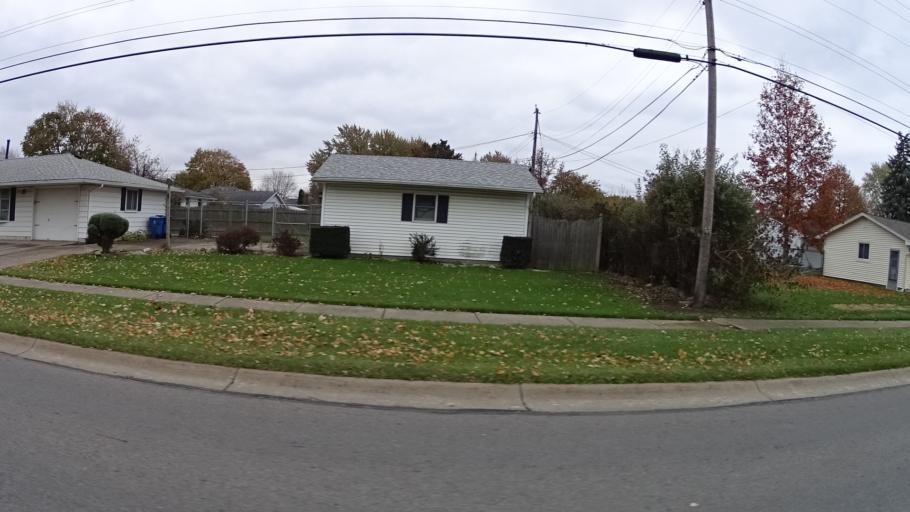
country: US
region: Ohio
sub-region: Lorain County
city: Lorain
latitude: 41.4344
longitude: -82.2041
